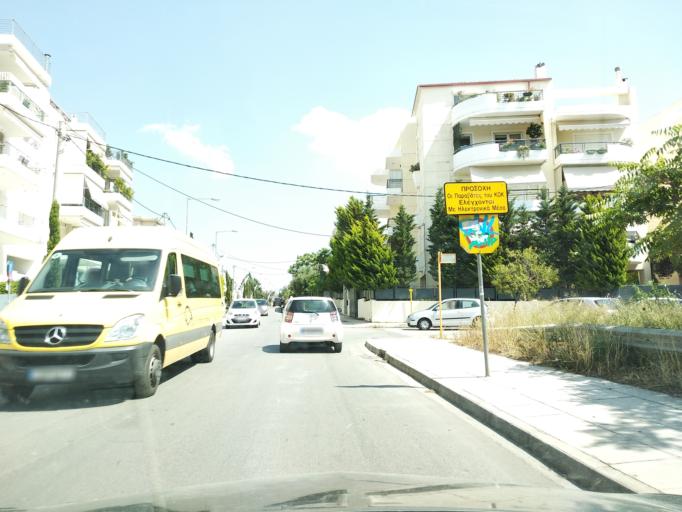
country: GR
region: Attica
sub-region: Nomarchia Athinas
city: Marousi
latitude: 38.0396
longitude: 23.7945
